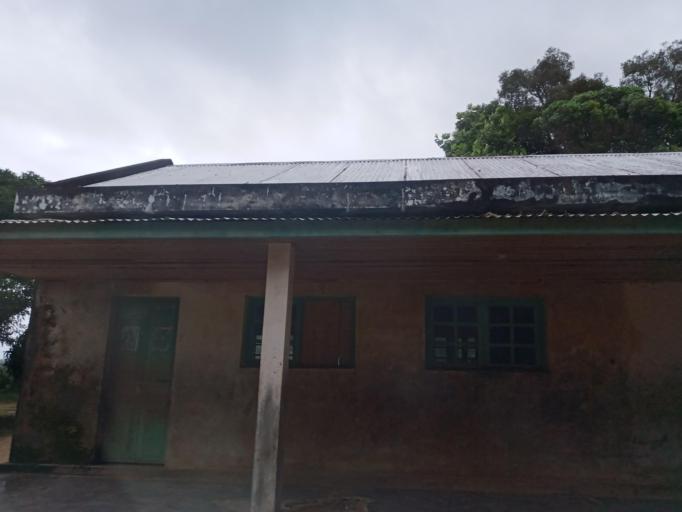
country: MG
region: Atsimo-Atsinanana
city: Vohipaho
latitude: -24.0445
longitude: 47.4392
